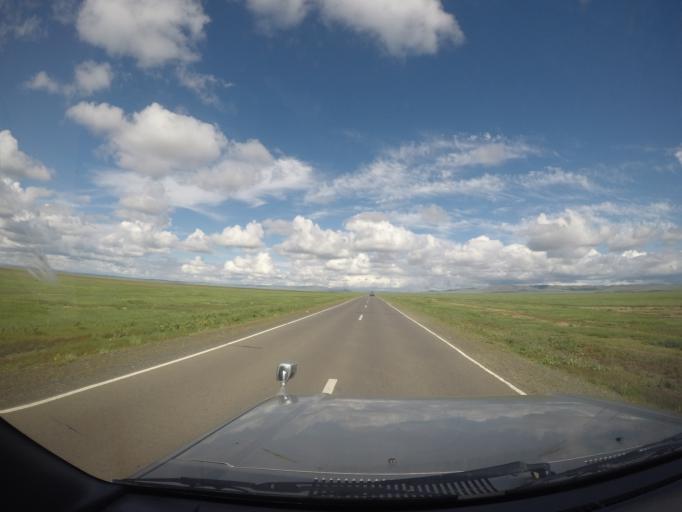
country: MN
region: Hentiy
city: Moron
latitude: 47.4194
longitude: 109.9830
